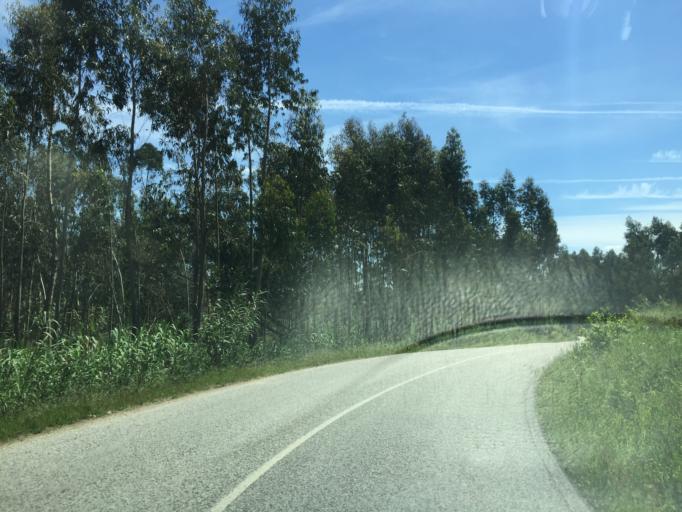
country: PT
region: Coimbra
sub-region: Figueira da Foz
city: Lavos
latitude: 40.0702
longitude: -8.7652
